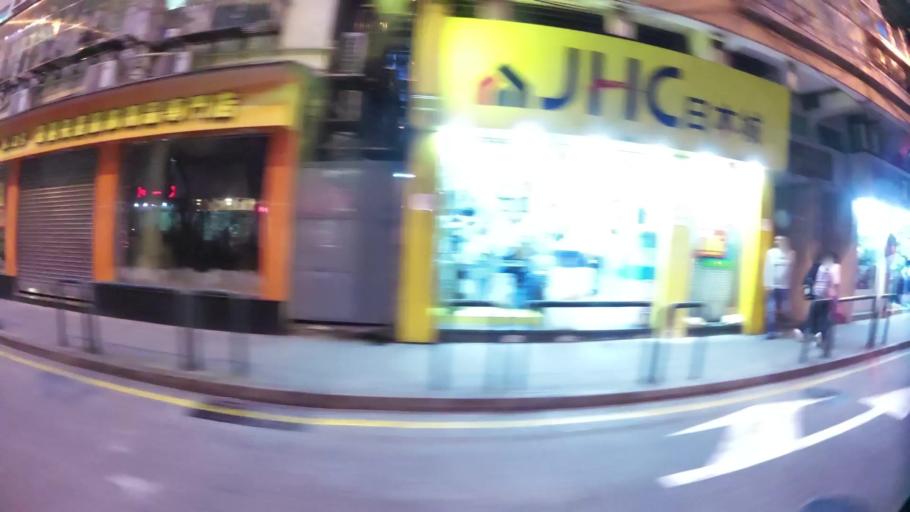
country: MO
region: Macau
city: Macau
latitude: 22.2047
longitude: 113.5471
